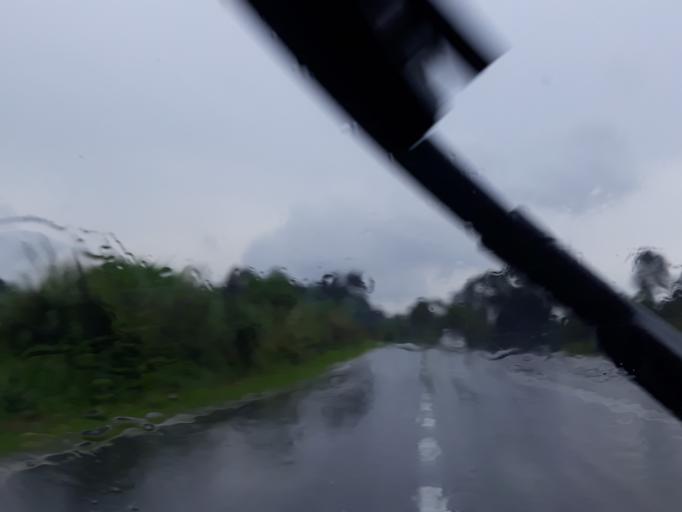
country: MY
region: Kedah
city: Kulim
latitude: 5.3525
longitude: 100.5839
